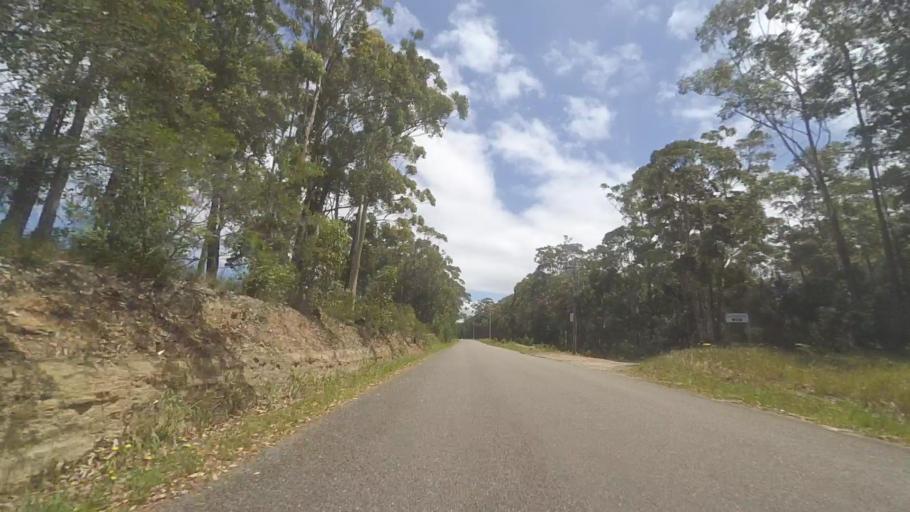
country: AU
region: New South Wales
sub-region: Shoalhaven Shire
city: Milton
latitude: -35.4069
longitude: 150.3584
